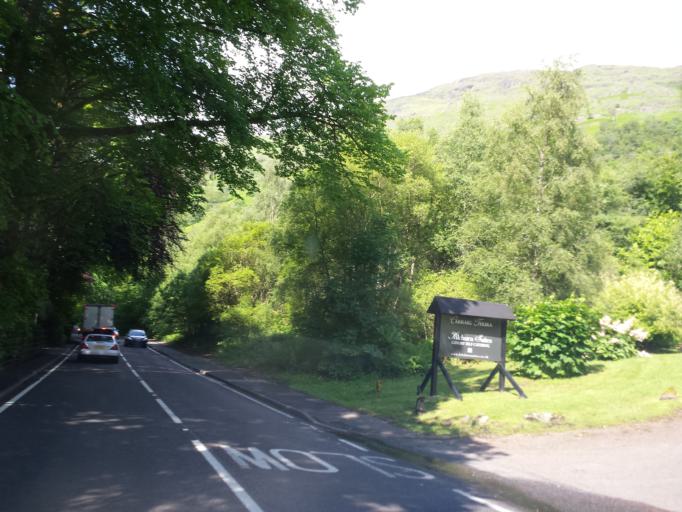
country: GB
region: Scotland
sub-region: Argyll and Bute
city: Garelochhead
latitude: 56.4040
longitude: -5.0378
